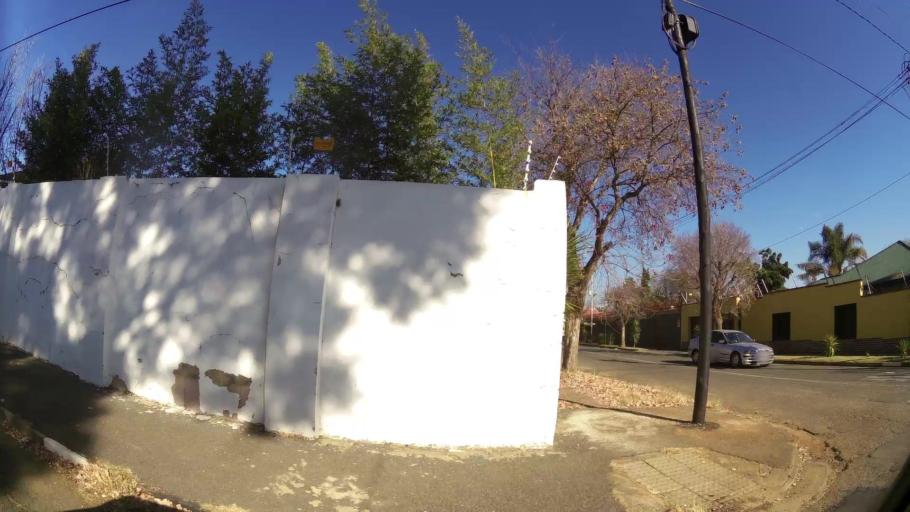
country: ZA
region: Gauteng
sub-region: City of Johannesburg Metropolitan Municipality
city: Johannesburg
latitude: -26.1854
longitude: 28.1106
